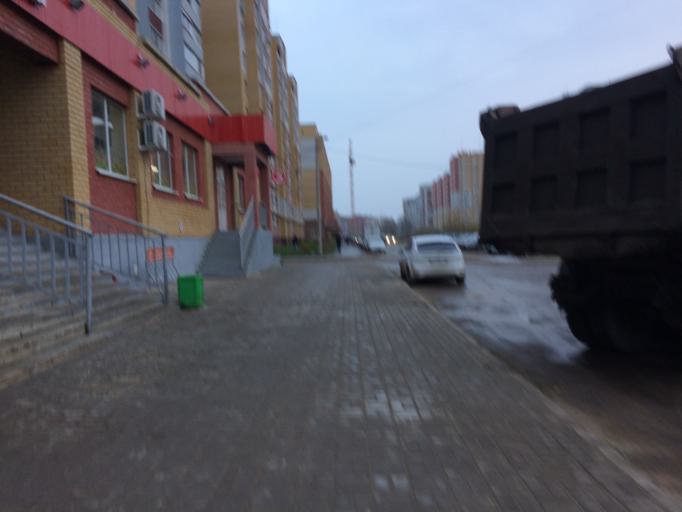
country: RU
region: Mariy-El
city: Yoshkar-Ola
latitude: 56.6396
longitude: 47.9246
